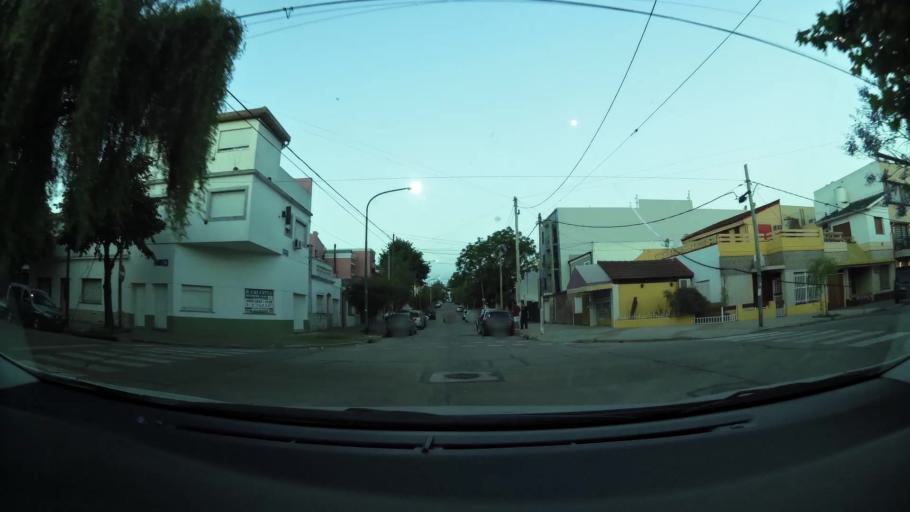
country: AR
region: Buenos Aires F.D.
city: Villa Lugano
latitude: -34.6821
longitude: -58.4736
